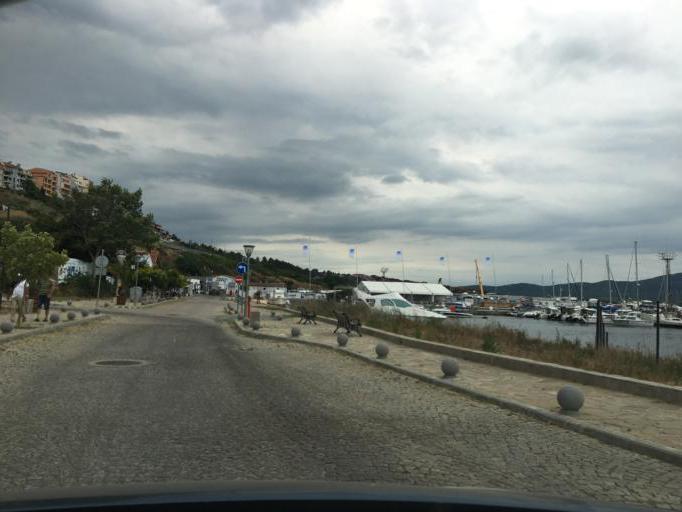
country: BG
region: Burgas
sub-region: Obshtina Sozopol
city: Sozopol
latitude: 42.4205
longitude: 27.6920
